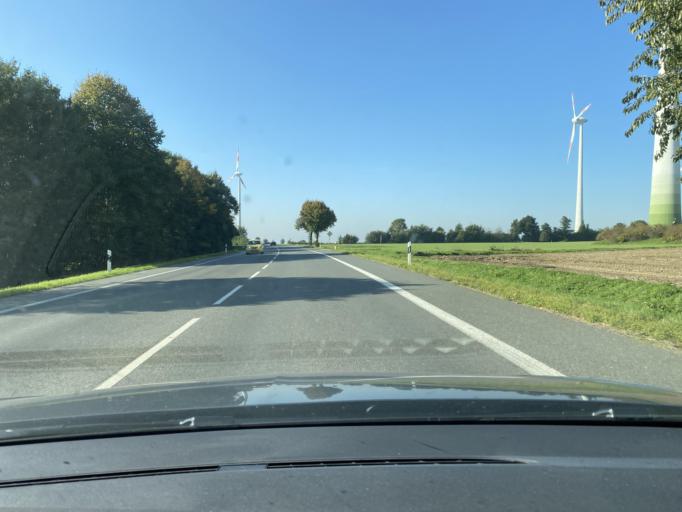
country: DE
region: North Rhine-Westphalia
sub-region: Regierungsbezirk Munster
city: Horstmar
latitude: 52.0901
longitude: 7.2722
